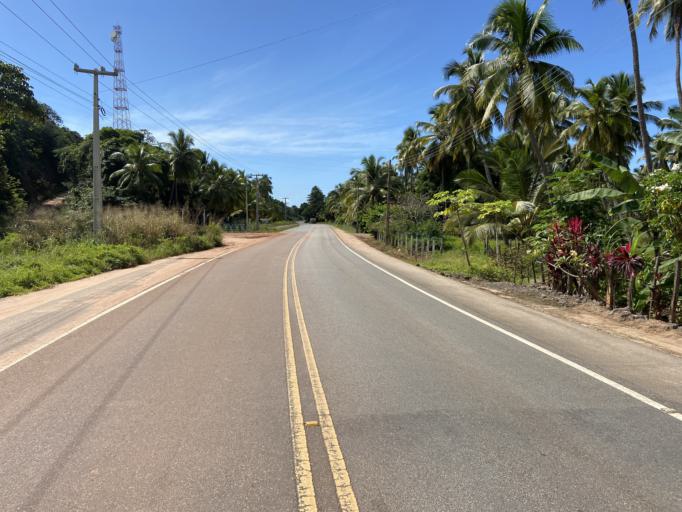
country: BR
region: Alagoas
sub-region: Coruripe
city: Coruripe
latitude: -10.2126
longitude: -36.2200
